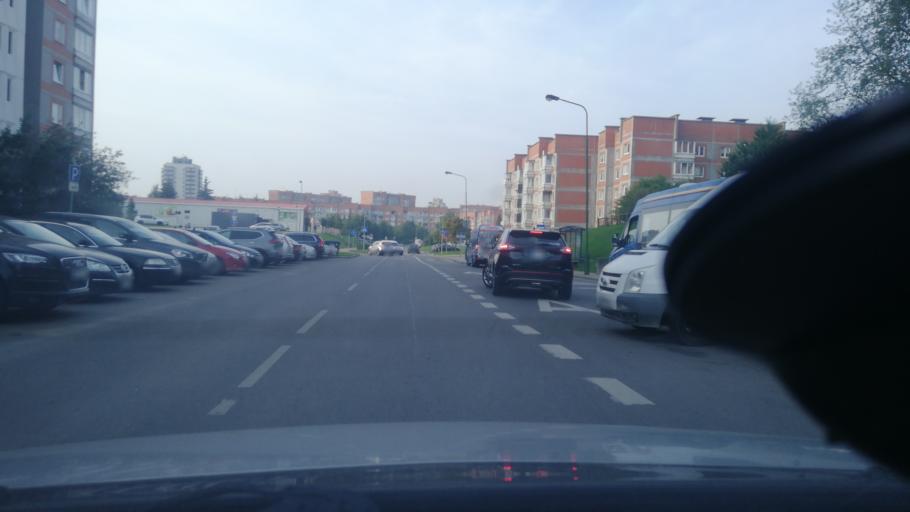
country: LT
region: Klaipedos apskritis
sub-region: Klaipeda
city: Klaipeda
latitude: 55.6625
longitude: 21.2015
